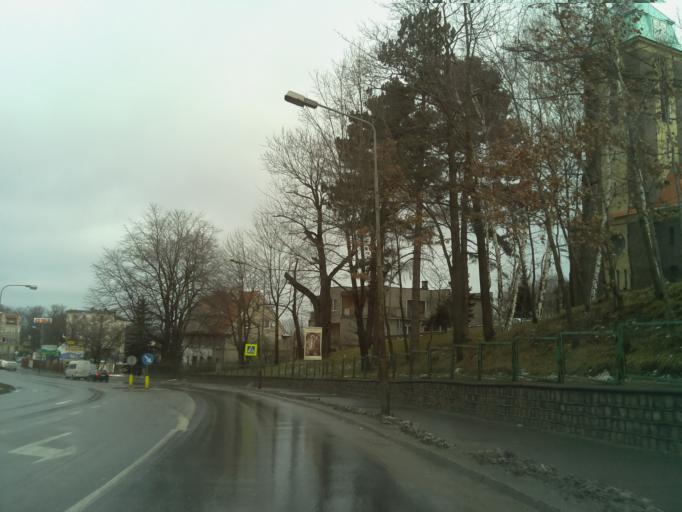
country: PL
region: Lower Silesian Voivodeship
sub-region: Powiat walbrzyski
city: Walbrzych
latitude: 50.8068
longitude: 16.2946
